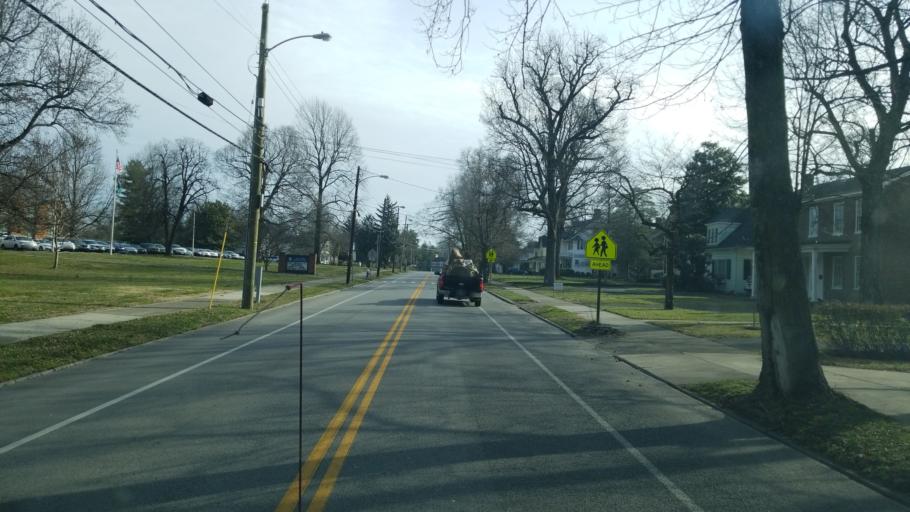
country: US
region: Kentucky
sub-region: Boyle County
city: Danville
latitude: 37.6487
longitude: -84.7679
